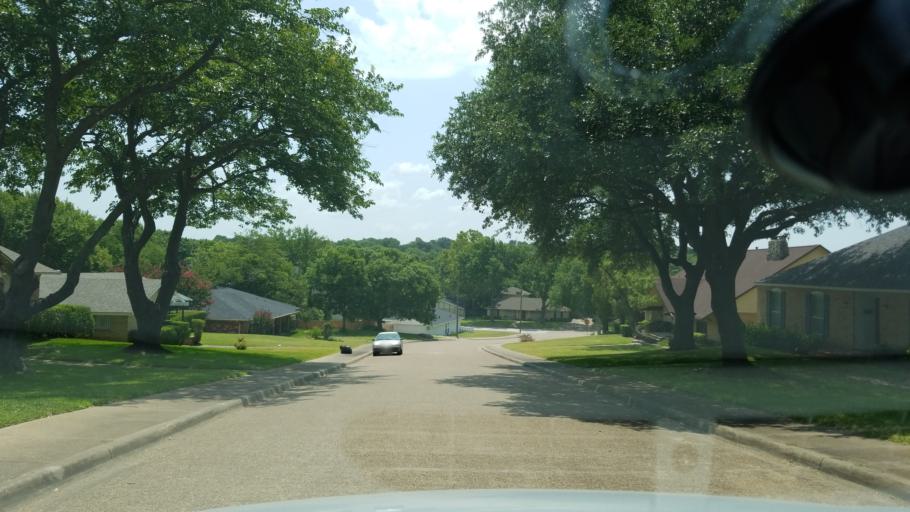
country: US
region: Texas
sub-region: Dallas County
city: Duncanville
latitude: 32.6760
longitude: -96.8377
